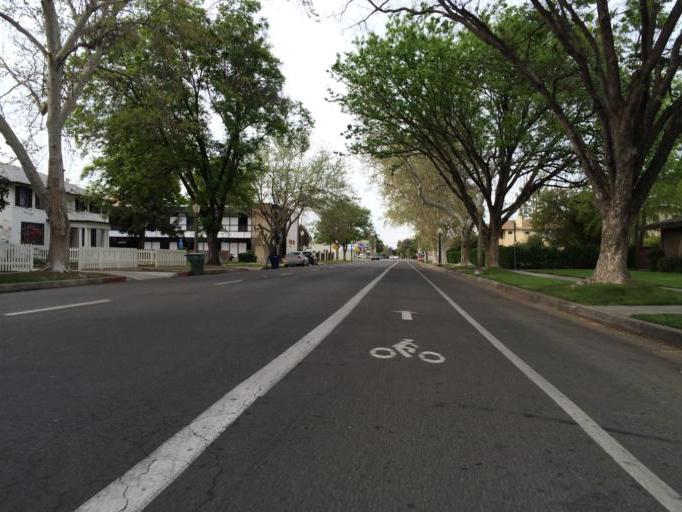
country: US
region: California
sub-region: Fresno County
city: Fresno
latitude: 36.7554
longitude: -119.7989
